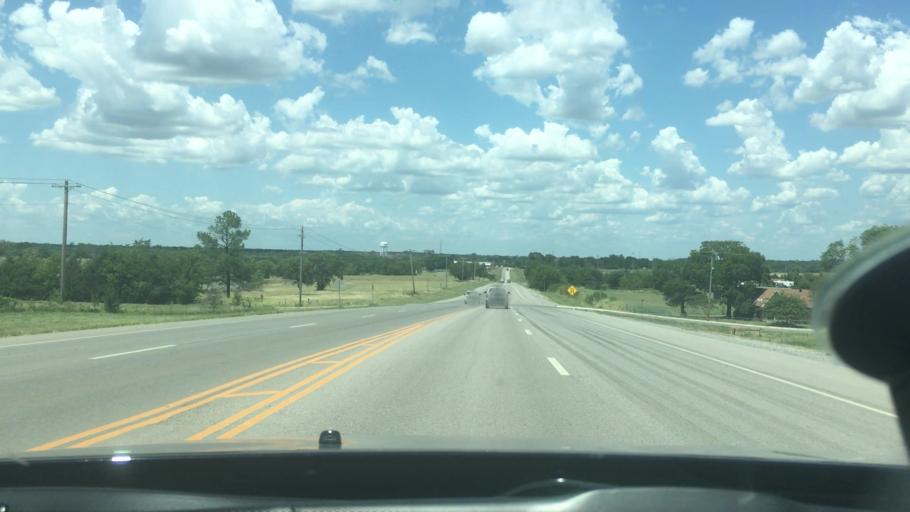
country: US
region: Oklahoma
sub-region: Bryan County
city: Durant
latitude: 33.9674
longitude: -96.3731
